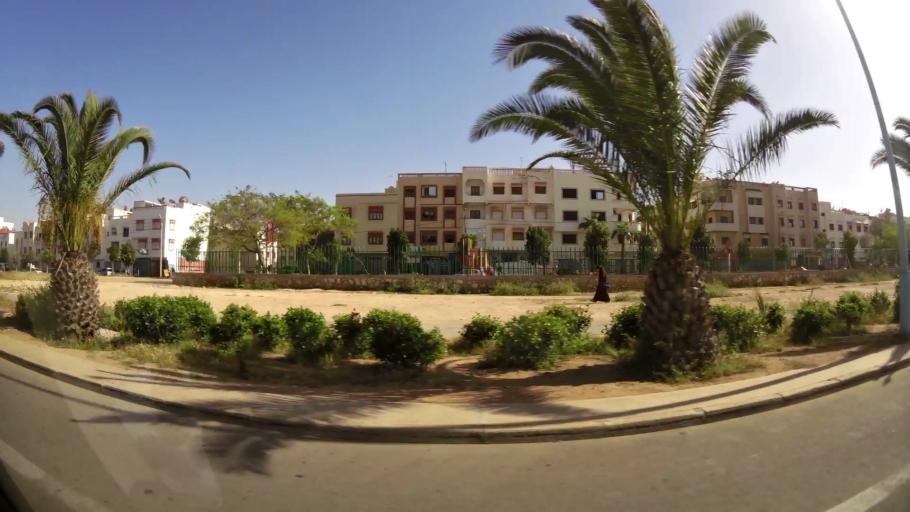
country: MA
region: Oued ed Dahab-Lagouira
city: Dakhla
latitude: 30.4038
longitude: -9.5523
